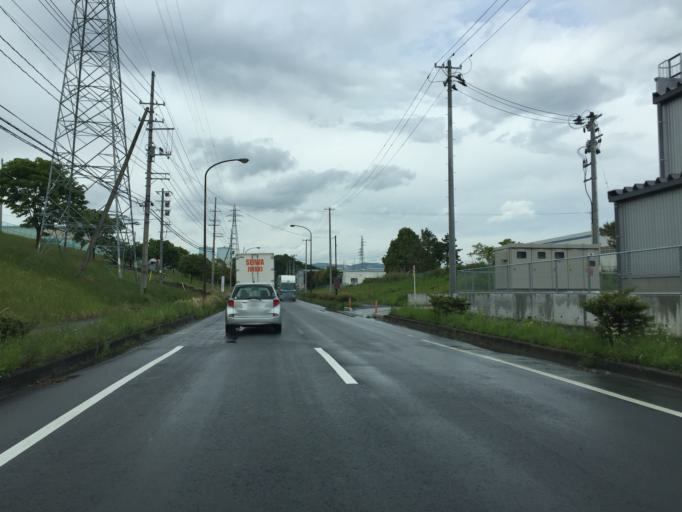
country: JP
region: Ibaraki
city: Kitaibaraki
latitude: 36.9372
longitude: 140.7469
